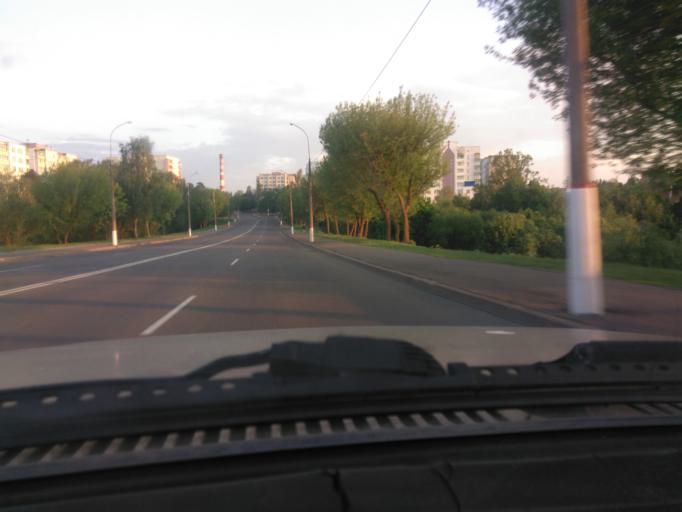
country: BY
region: Mogilev
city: Mahilyow
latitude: 53.9233
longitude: 30.3118
